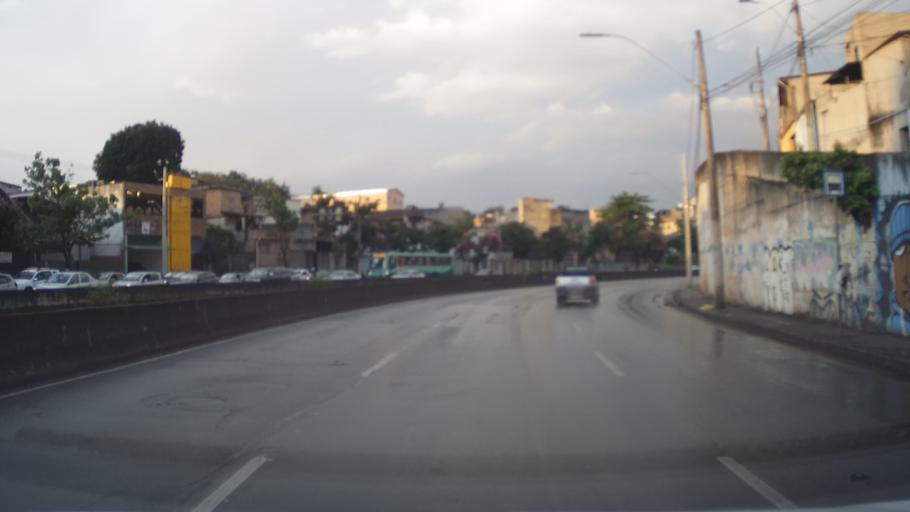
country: BR
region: Minas Gerais
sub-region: Belo Horizonte
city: Belo Horizonte
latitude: -19.9537
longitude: -43.9855
